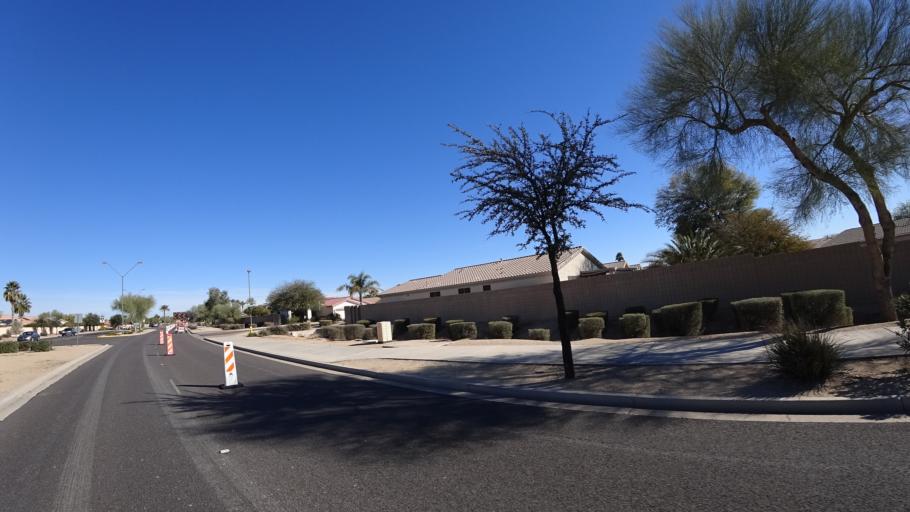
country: US
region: Arizona
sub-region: Maricopa County
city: Litchfield Park
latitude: 33.4807
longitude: -112.3752
